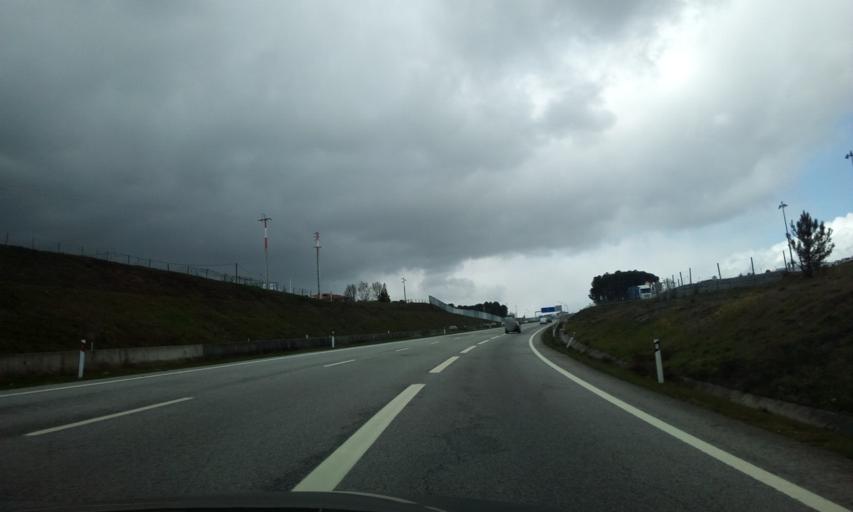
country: PT
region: Viseu
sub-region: Viseu
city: Rio de Loba
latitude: 40.6325
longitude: -7.8437
